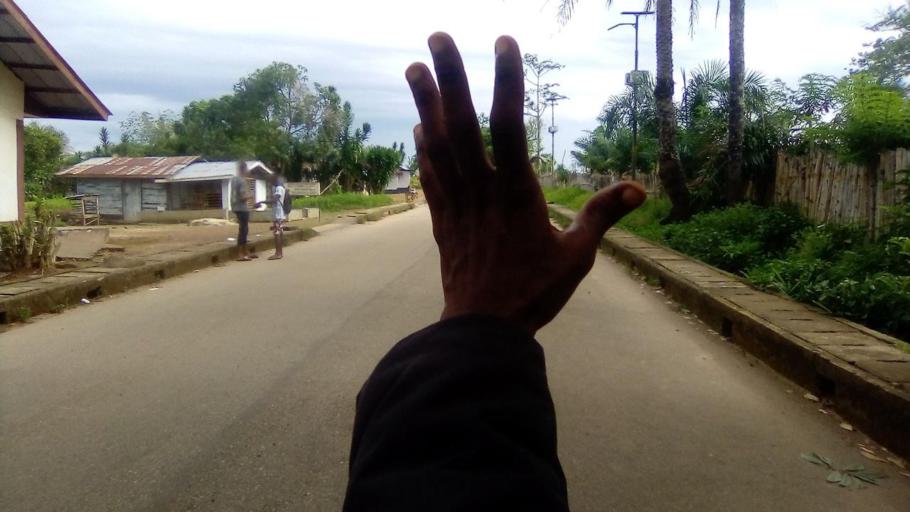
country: SL
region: Southern Province
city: Pujehun
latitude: 7.3664
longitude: -11.7257
